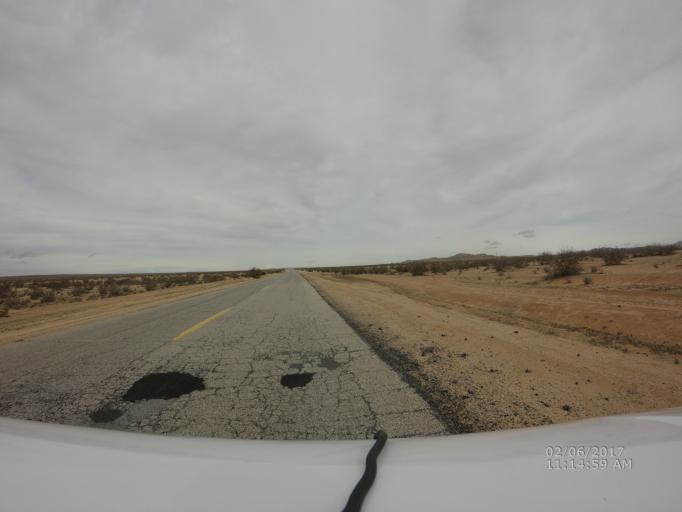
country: US
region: California
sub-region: Los Angeles County
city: Lake Los Angeles
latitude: 34.6649
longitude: -117.7022
